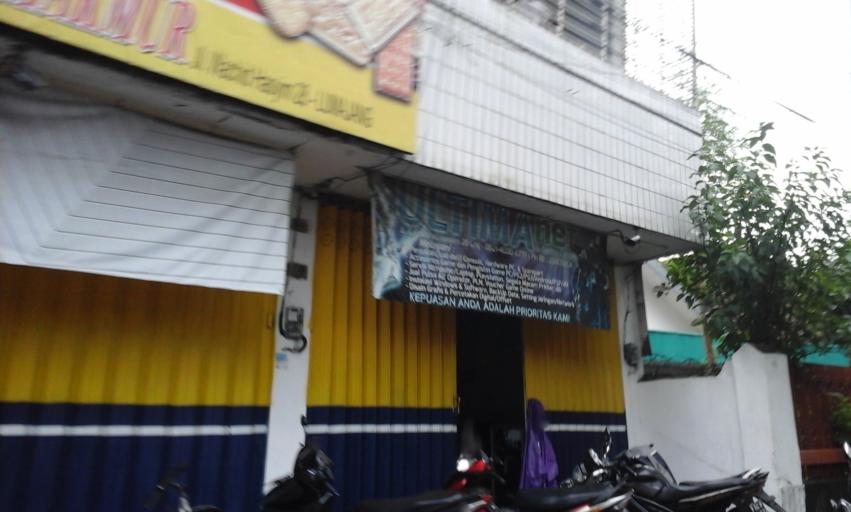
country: ID
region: East Java
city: Lumajang
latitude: -8.1305
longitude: 113.2209
